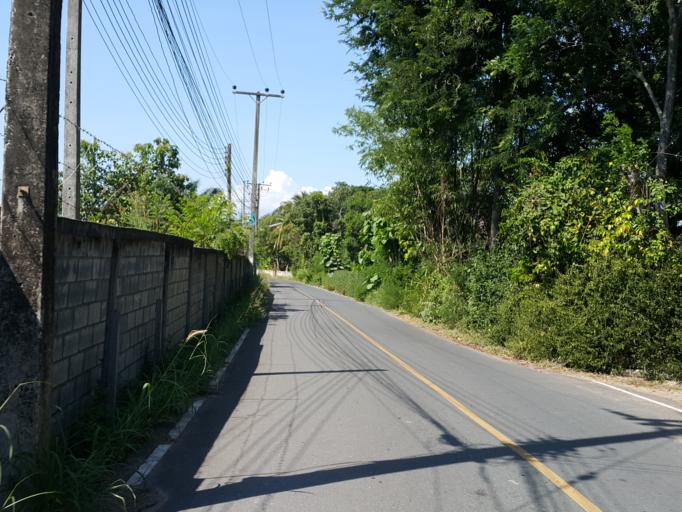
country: TH
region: Chiang Mai
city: San Sai
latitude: 18.8533
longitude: 99.1459
